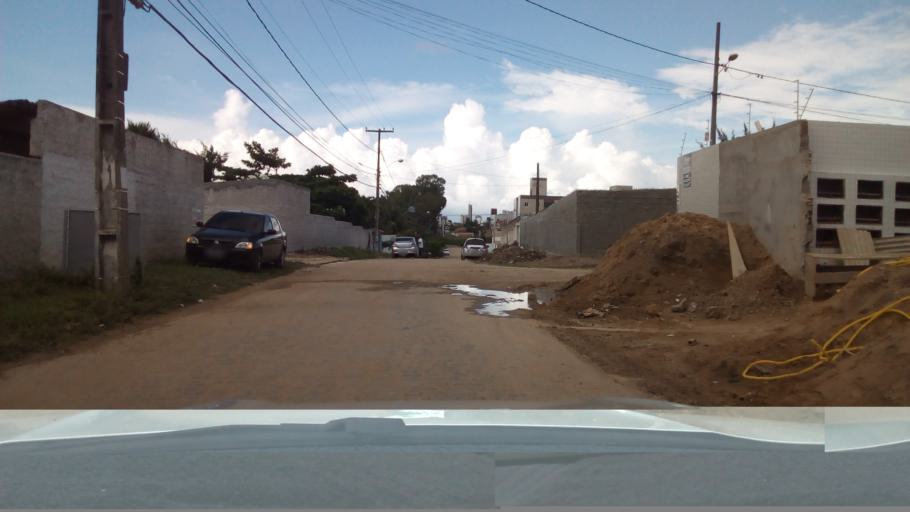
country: BR
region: Paraiba
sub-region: Joao Pessoa
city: Joao Pessoa
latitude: -7.1602
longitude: -34.8510
